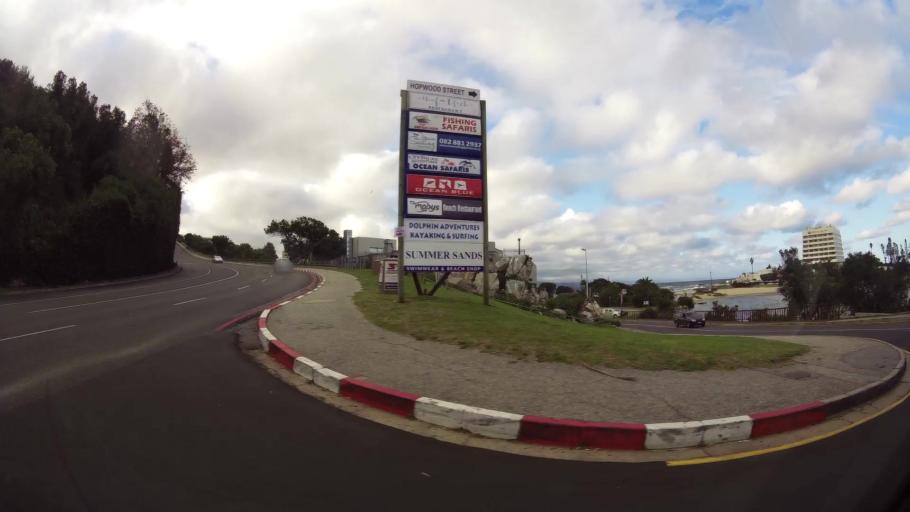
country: ZA
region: Western Cape
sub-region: Eden District Municipality
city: Plettenberg Bay
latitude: -34.0605
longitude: 23.3760
